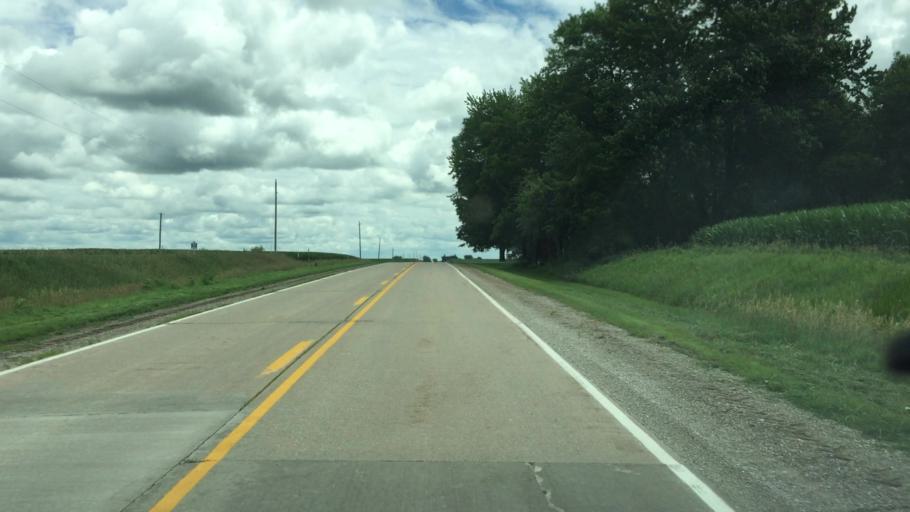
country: US
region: Iowa
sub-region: Jasper County
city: Monroe
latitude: 41.5807
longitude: -93.1421
